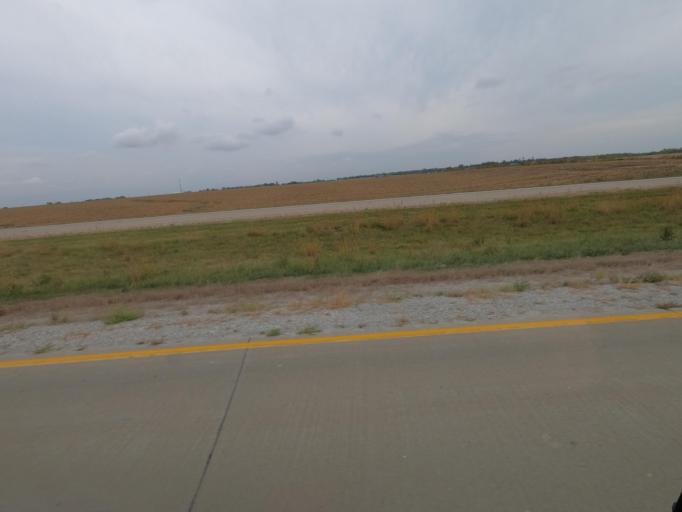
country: US
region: Iowa
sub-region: Jasper County
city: Monroe
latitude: 41.5308
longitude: -93.1304
